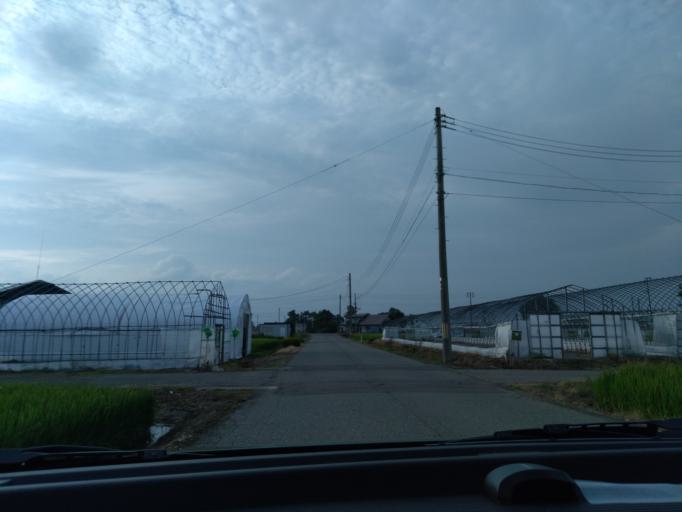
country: JP
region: Akita
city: Omagari
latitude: 39.4071
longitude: 140.5136
